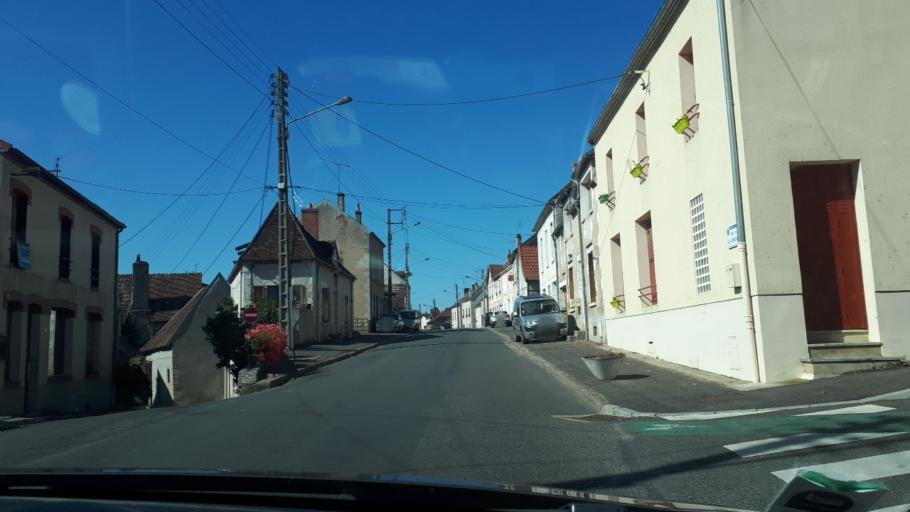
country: FR
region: Centre
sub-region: Departement du Loiret
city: Briare
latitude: 47.5894
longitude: 2.7444
